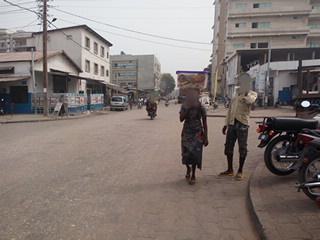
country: BJ
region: Littoral
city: Cotonou
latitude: 6.3597
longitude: 2.4249
